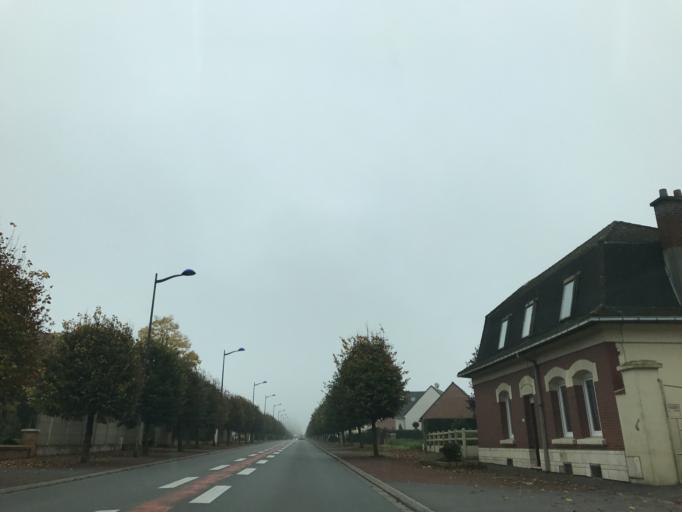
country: FR
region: Nord-Pas-de-Calais
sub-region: Departement du Pas-de-Calais
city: Bapaume
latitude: 50.0965
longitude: 2.8593
